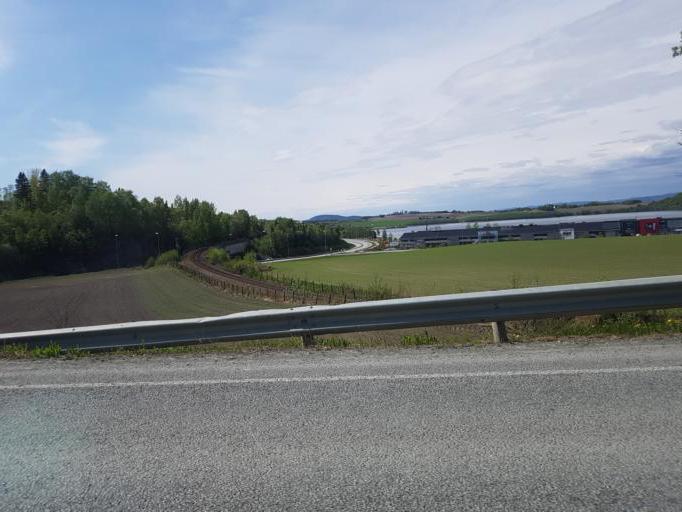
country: NO
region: Nord-Trondelag
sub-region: Levanger
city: Levanger
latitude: 63.7325
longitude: 11.2897
